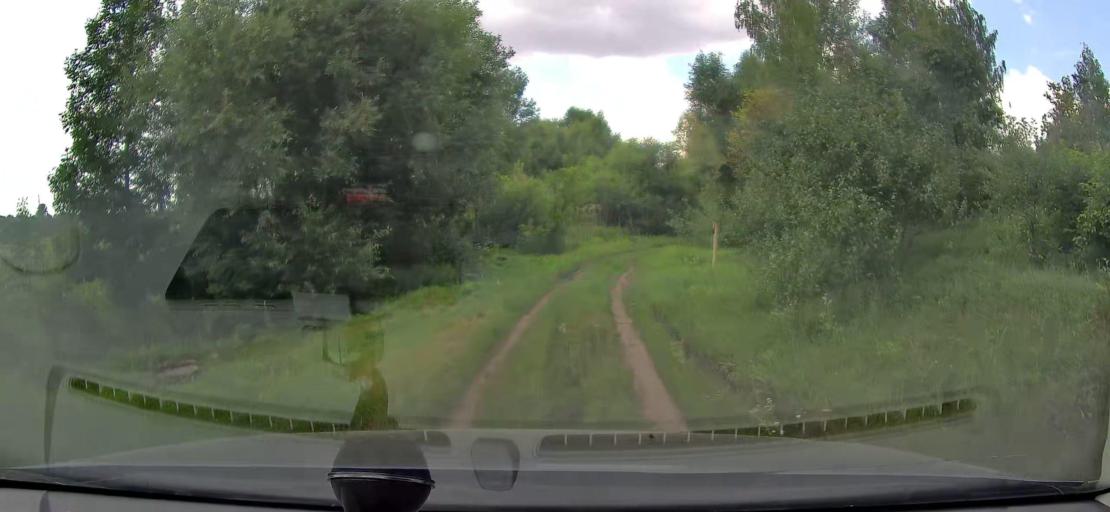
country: RU
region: Kursk
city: Zolotukhino
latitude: 52.0309
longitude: 36.1985
